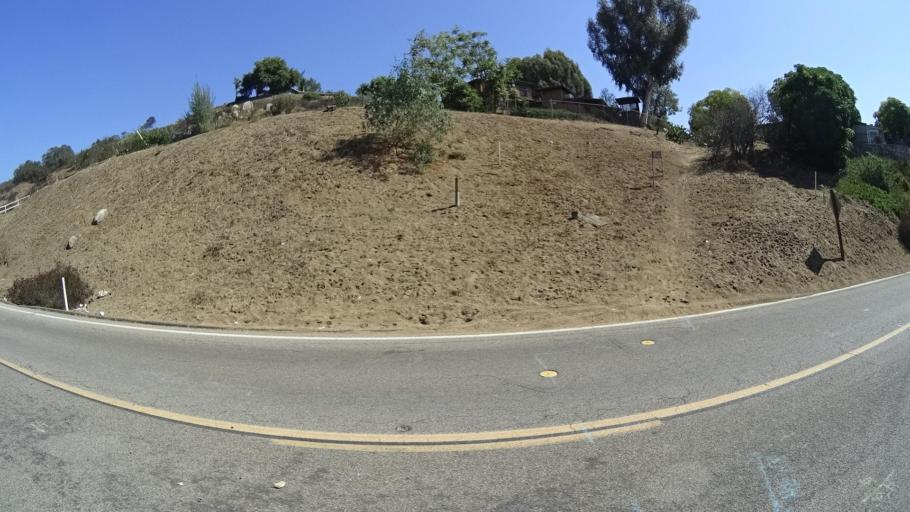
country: US
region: California
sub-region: San Diego County
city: Granite Hills
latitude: 32.8097
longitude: -116.9076
